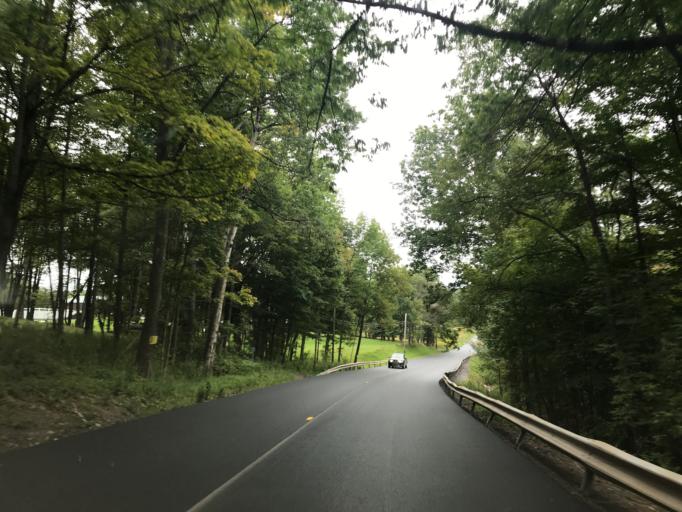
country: US
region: New York
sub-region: Delaware County
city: Stamford
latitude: 42.5281
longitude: -74.6215
